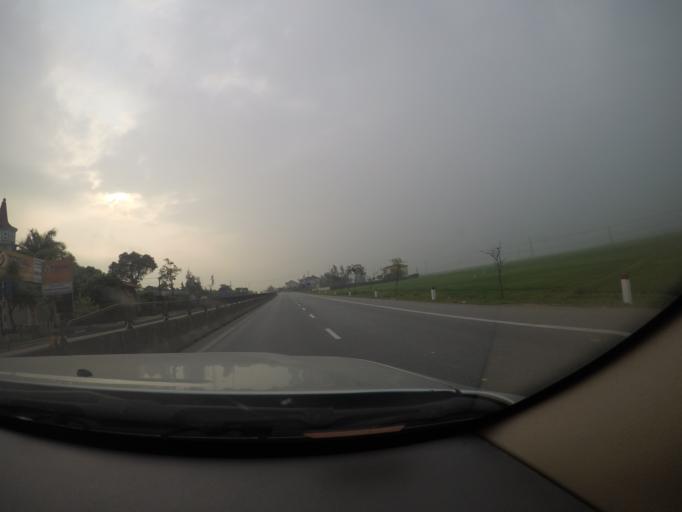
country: VN
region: Ha Tinh
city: Cam Xuyen
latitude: 18.2359
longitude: 106.0222
